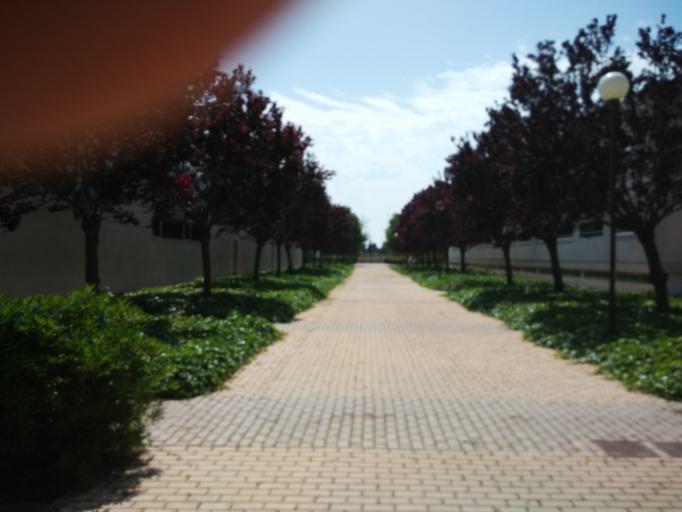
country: ES
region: Valencia
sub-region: Provincia de Alicante
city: San Vicent del Raspeig
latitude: 38.3829
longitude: -0.5121
